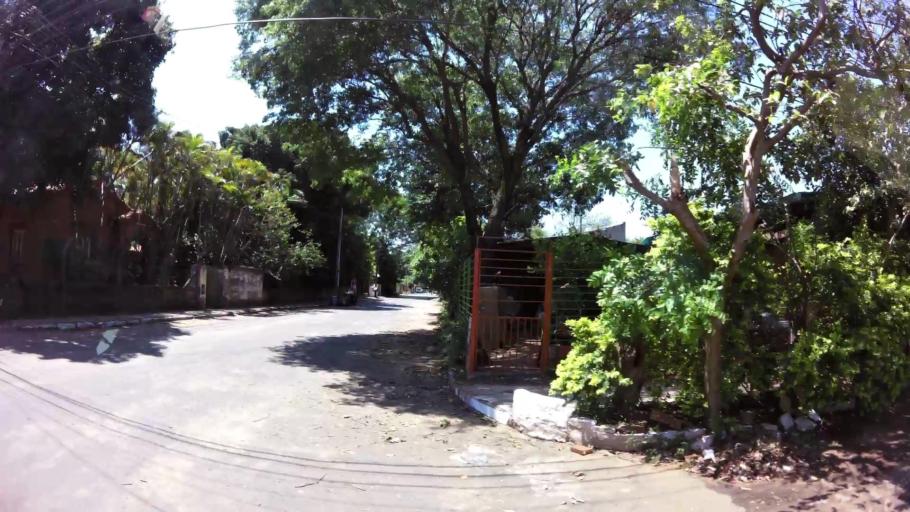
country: PY
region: Central
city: Fernando de la Mora
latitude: -25.3260
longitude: -57.5585
